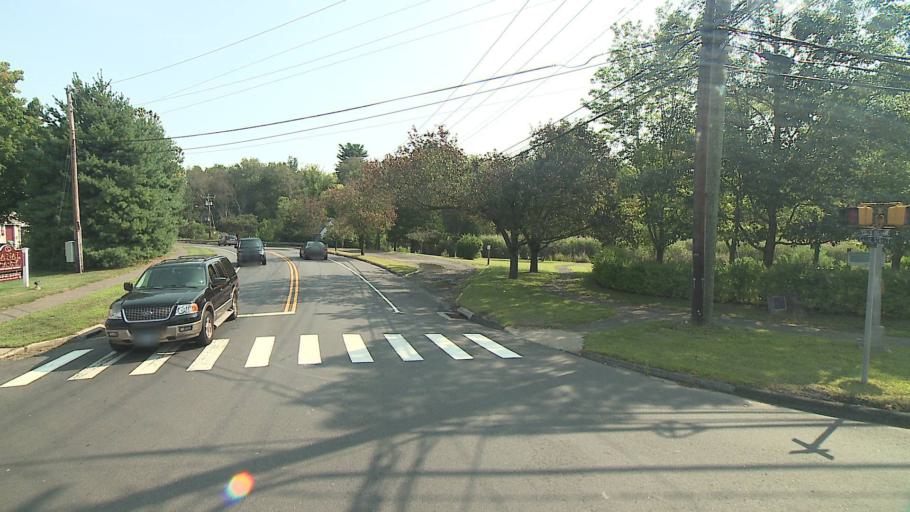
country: US
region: Connecticut
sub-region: Fairfield County
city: Westport
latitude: 41.1475
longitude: -73.3638
